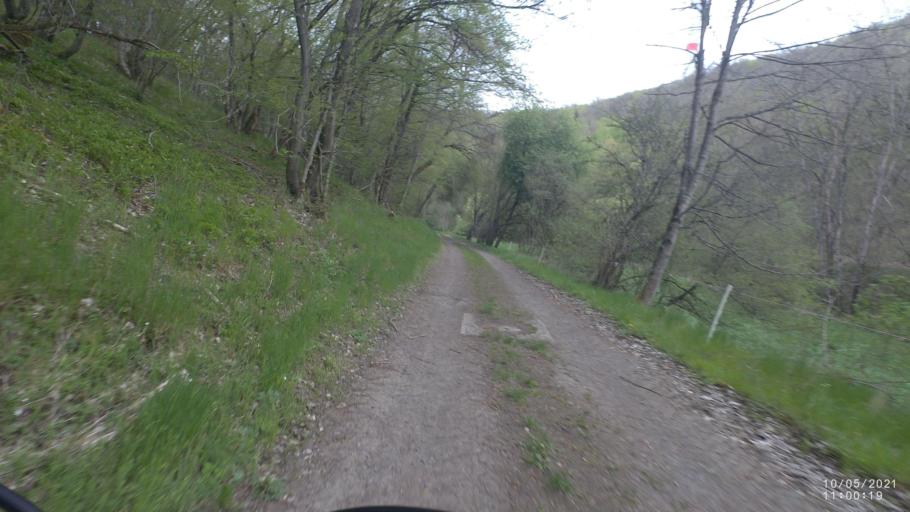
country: DE
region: Rheinland-Pfalz
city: Reudelsterz
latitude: 50.3045
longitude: 7.1384
